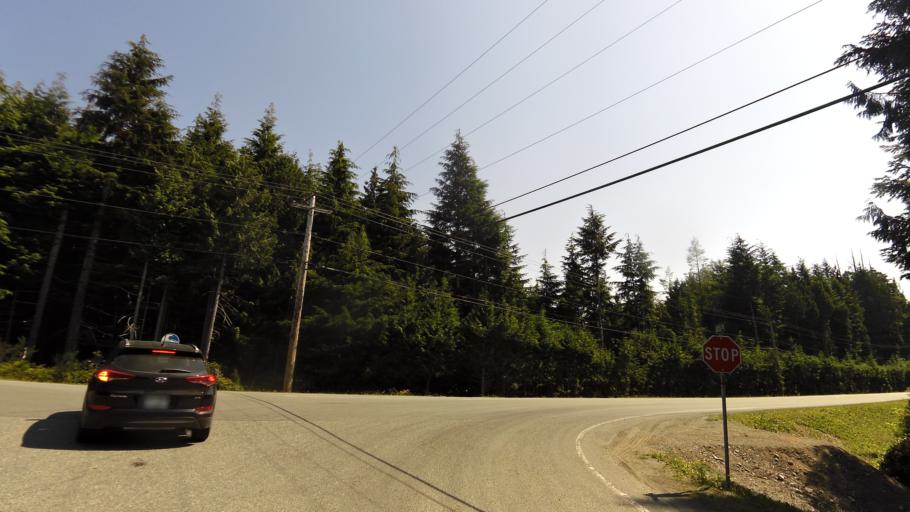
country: CA
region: British Columbia
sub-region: Regional District of Alberni-Clayoquot
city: Ucluelet
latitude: 49.0204
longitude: -125.6372
